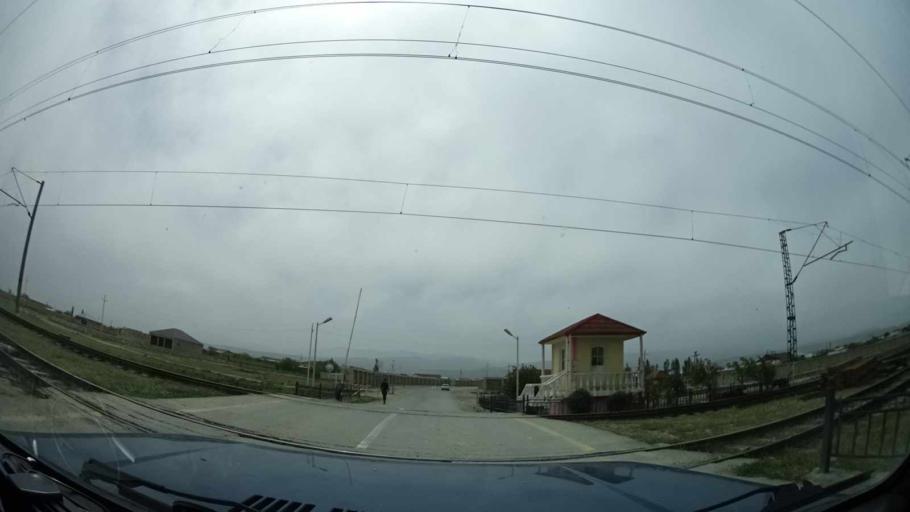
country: AZ
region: Xizi
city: Kilyazi
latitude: 40.8672
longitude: 49.3492
